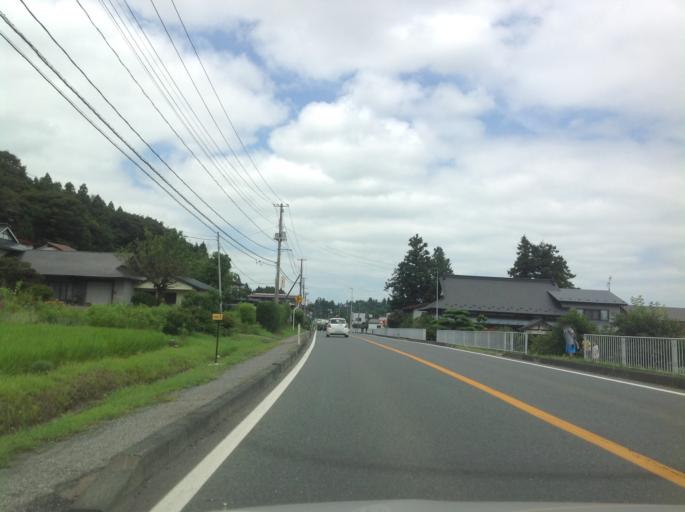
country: JP
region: Iwate
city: Mizusawa
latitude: 39.0888
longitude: 141.1365
